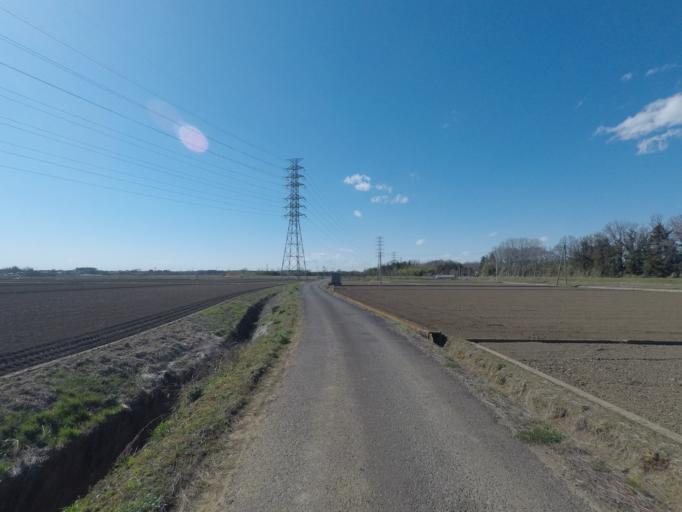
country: JP
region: Ibaraki
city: Tsukuba
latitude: 36.1418
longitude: 140.1133
